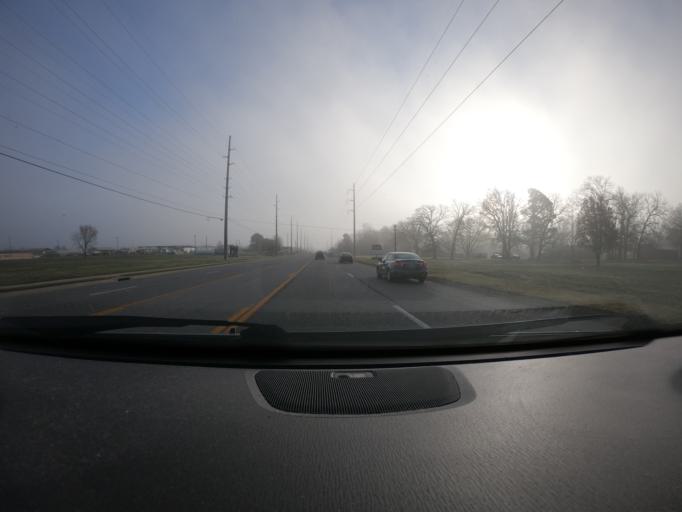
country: US
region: Arkansas
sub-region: Benton County
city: Bentonville
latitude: 36.3573
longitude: -94.2307
